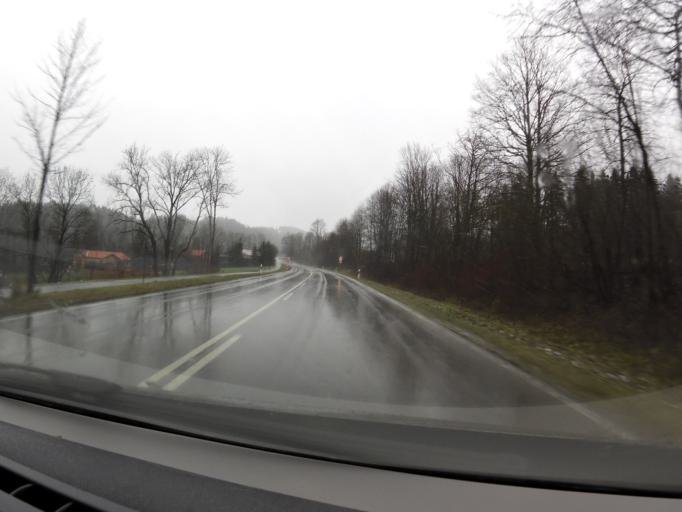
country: DE
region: Bavaria
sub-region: Upper Bavaria
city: Bad Heilbrunn
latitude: 47.7467
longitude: 11.4777
